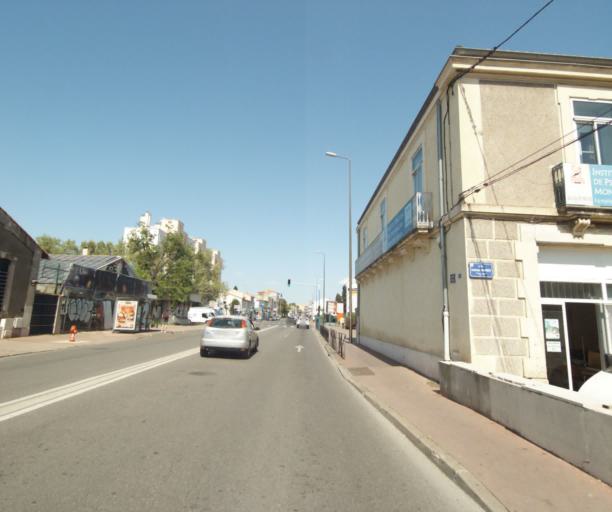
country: FR
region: Languedoc-Roussillon
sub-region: Departement de l'Herault
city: Montpellier
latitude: 43.5969
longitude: 3.8637
